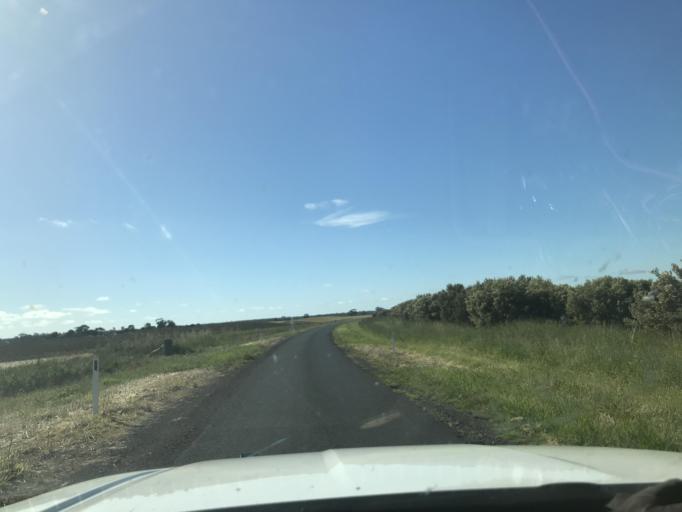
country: AU
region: Victoria
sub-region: Horsham
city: Horsham
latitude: -37.0510
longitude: 141.7470
